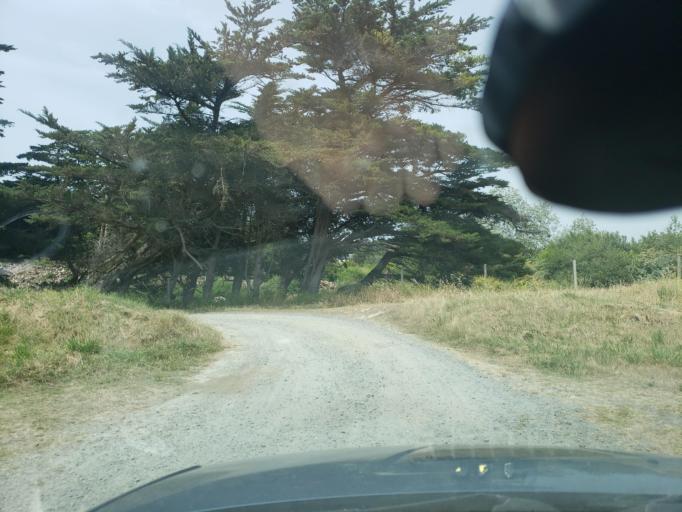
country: FR
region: Brittany
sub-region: Departement du Finistere
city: Guilvinec
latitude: 47.8009
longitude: -4.3170
